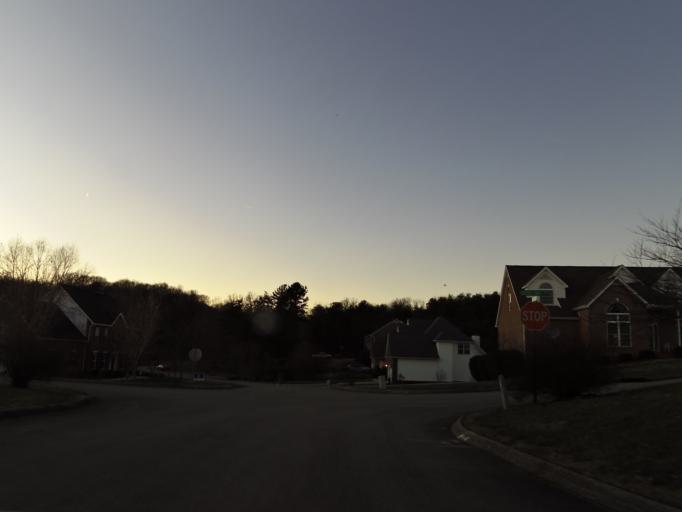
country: US
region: Tennessee
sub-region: Blount County
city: Eagleton Village
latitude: 35.8776
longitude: -83.9424
